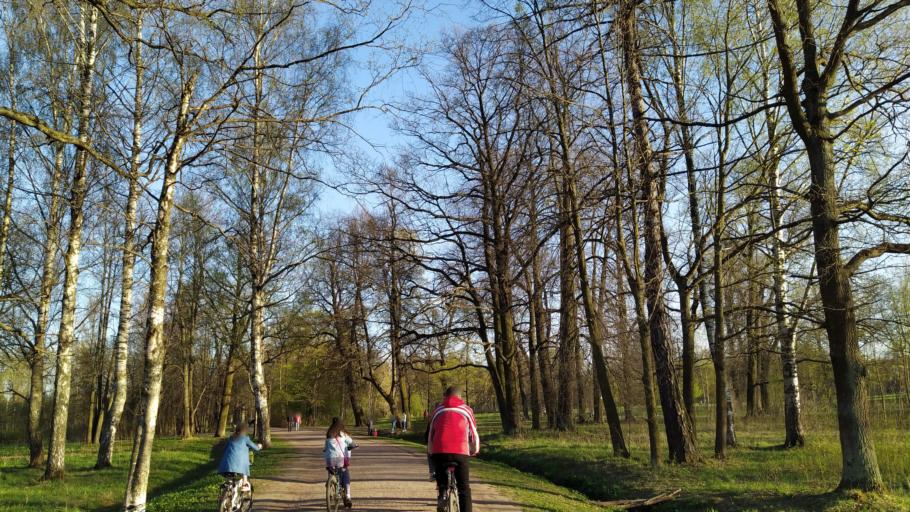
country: RU
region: St.-Petersburg
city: Pavlovsk
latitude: 59.7042
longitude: 30.4256
